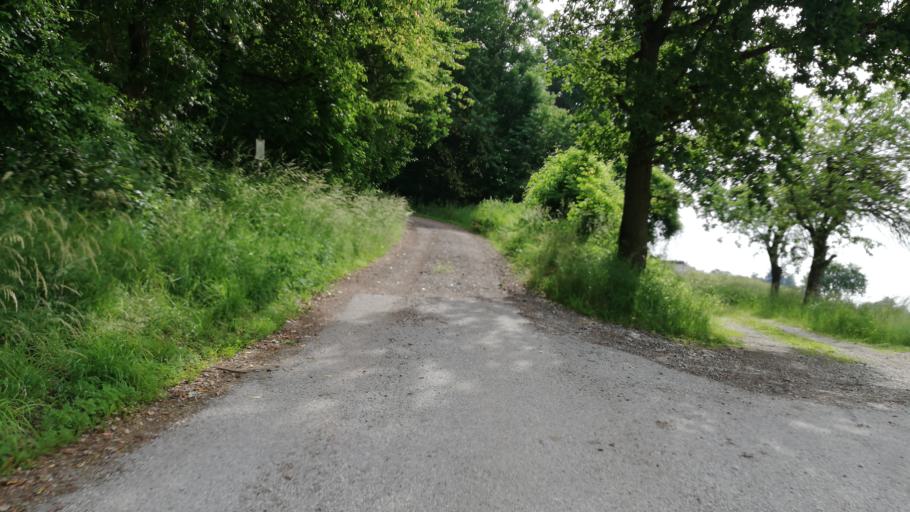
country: AT
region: Upper Austria
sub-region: Politischer Bezirk Grieskirchen
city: Bad Schallerbach
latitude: 48.2395
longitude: 13.9257
